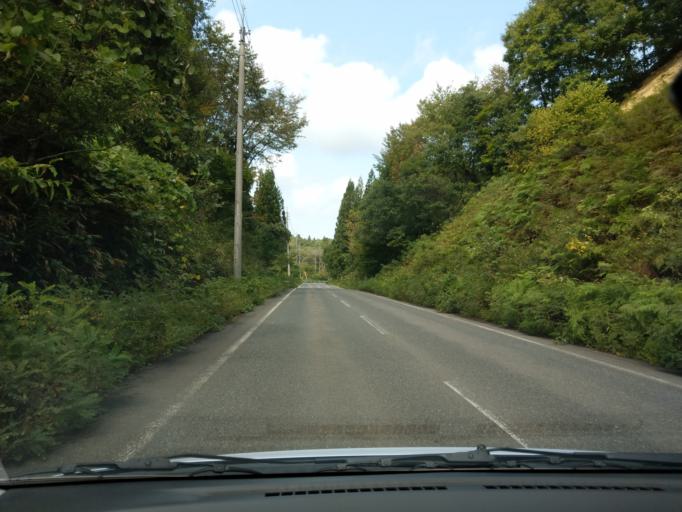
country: JP
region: Akita
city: Omagari
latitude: 39.4606
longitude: 140.3183
